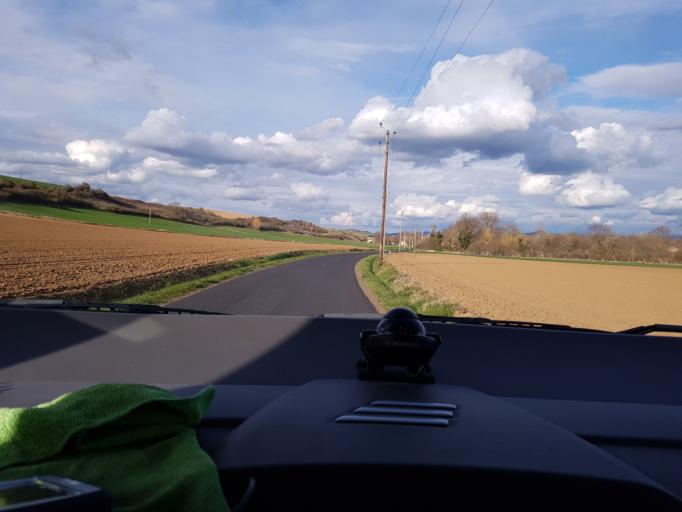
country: FR
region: Auvergne
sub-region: Departement du Puy-de-Dome
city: Saint-Germain-Lembron
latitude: 45.4550
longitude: 3.2148
